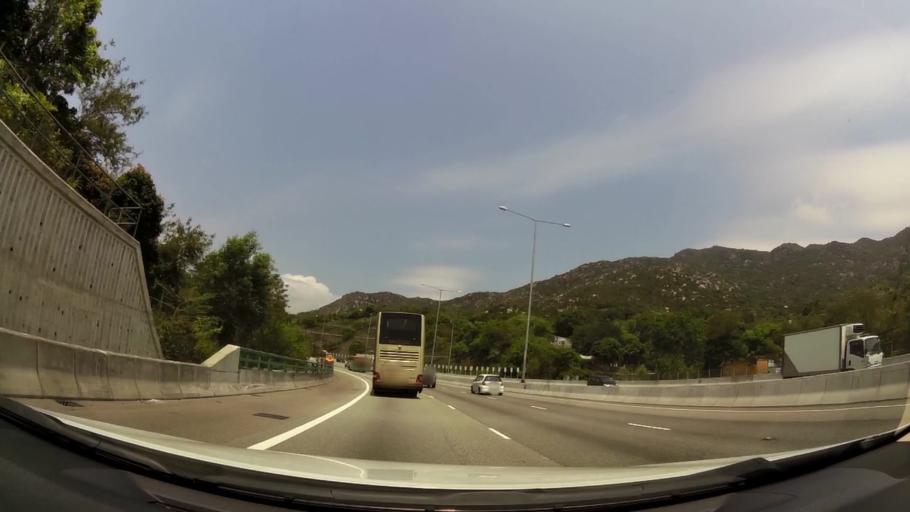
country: HK
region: Tuen Mun
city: Tuen Mun
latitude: 22.3752
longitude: 113.9961
